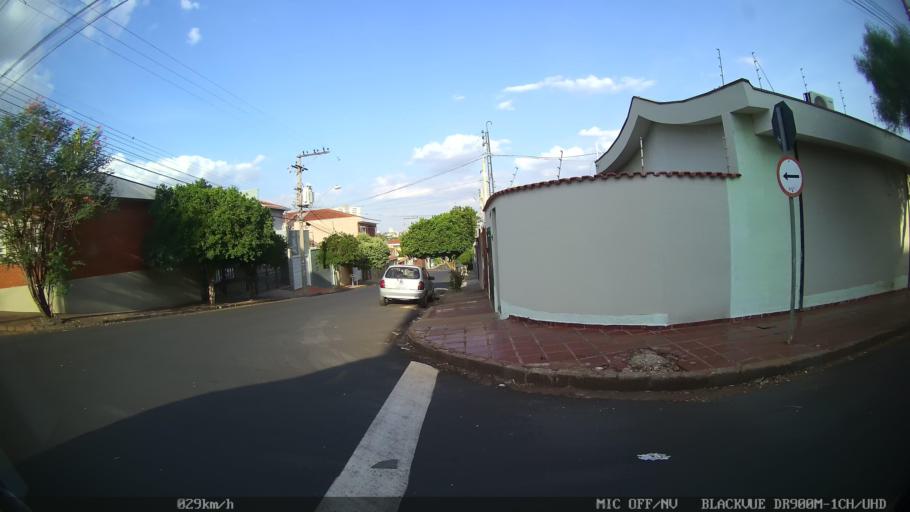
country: BR
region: Sao Paulo
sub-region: Ribeirao Preto
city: Ribeirao Preto
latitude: -21.1734
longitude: -47.8355
